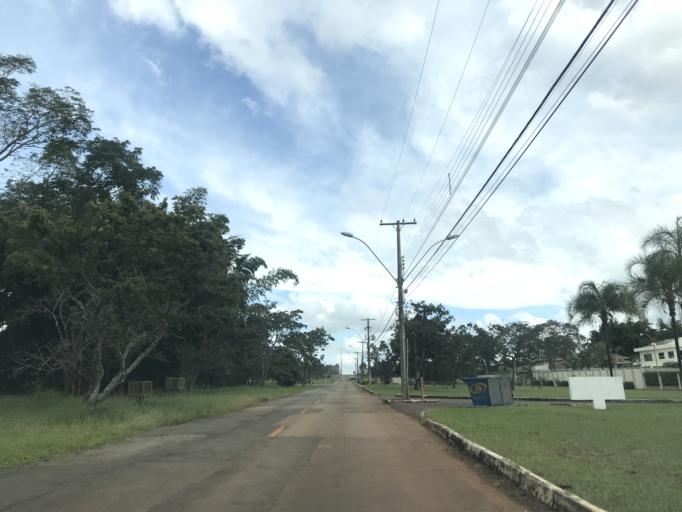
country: BR
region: Federal District
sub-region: Brasilia
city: Brasilia
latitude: -15.8966
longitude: -47.9262
